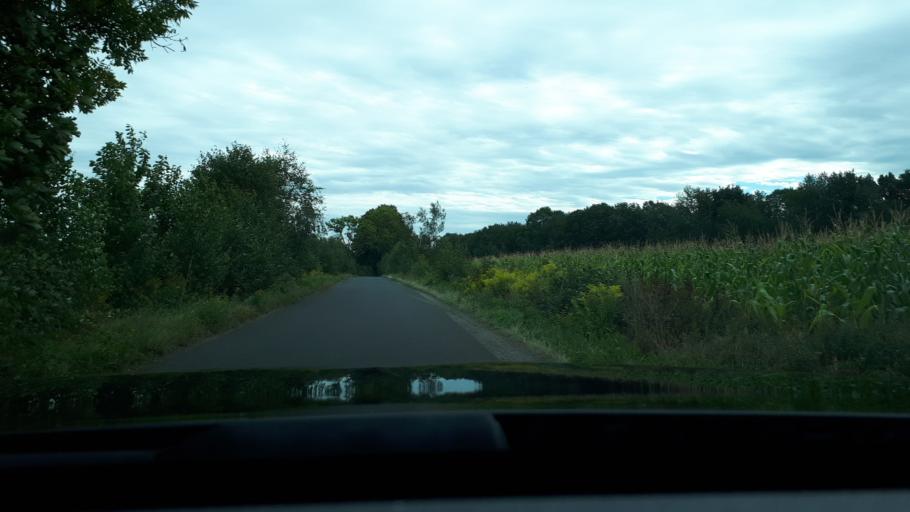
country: PL
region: Lower Silesian Voivodeship
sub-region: Powiat lubanski
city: Olszyna
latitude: 51.0355
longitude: 15.3289
